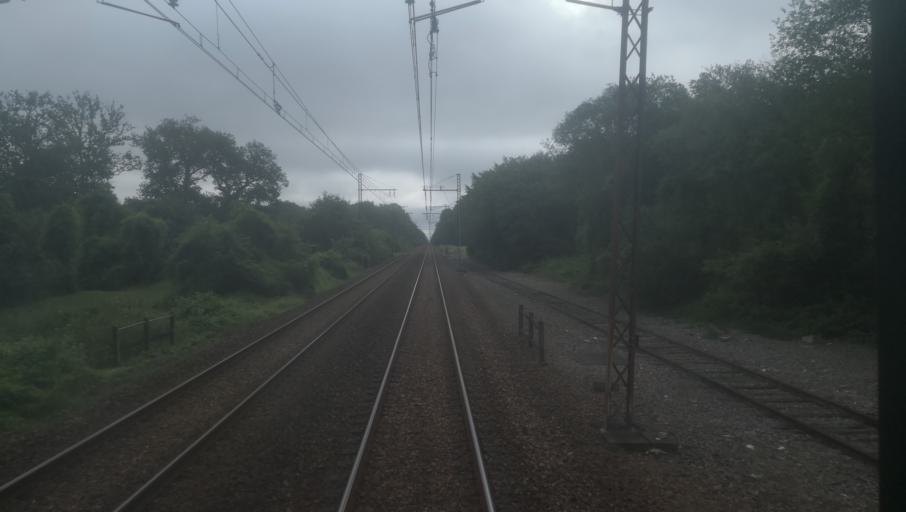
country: FR
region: Centre
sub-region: Departement de l'Indre
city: Montierchaume
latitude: 46.8515
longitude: 1.7960
